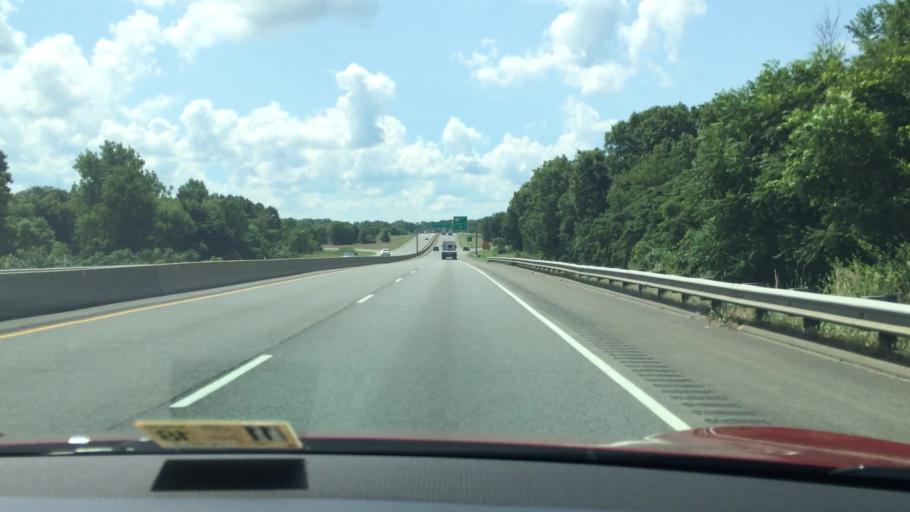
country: US
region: Indiana
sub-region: Saint Joseph County
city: South Bend
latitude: 41.6781
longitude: -86.3410
